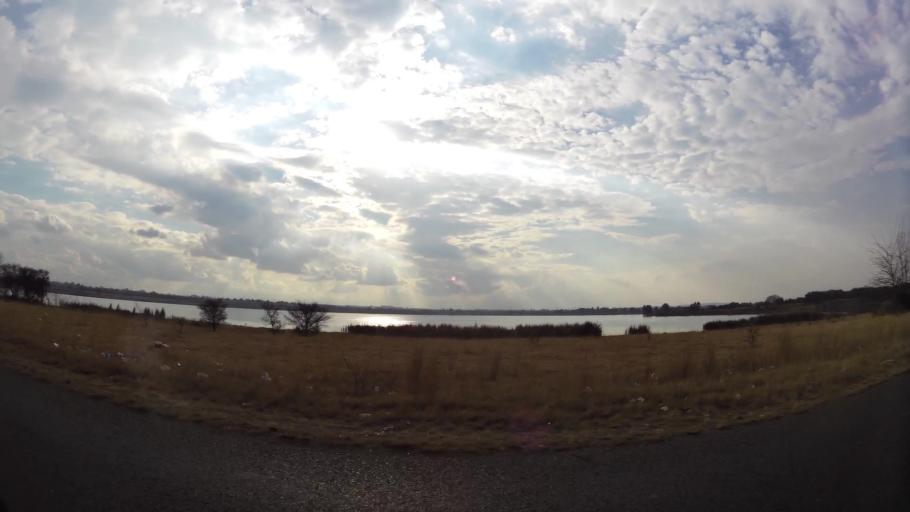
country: ZA
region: Gauteng
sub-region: Sedibeng District Municipality
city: Vereeniging
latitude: -26.6918
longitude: 27.8975
